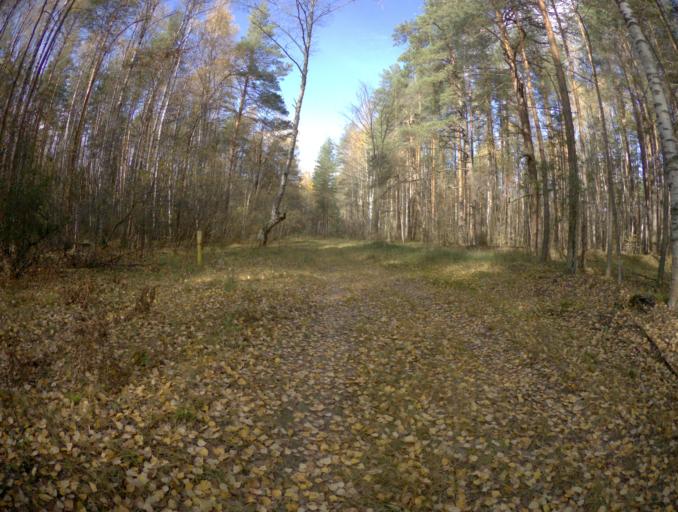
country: RU
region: Vladimir
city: Kommunar
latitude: 56.0774
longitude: 40.4430
